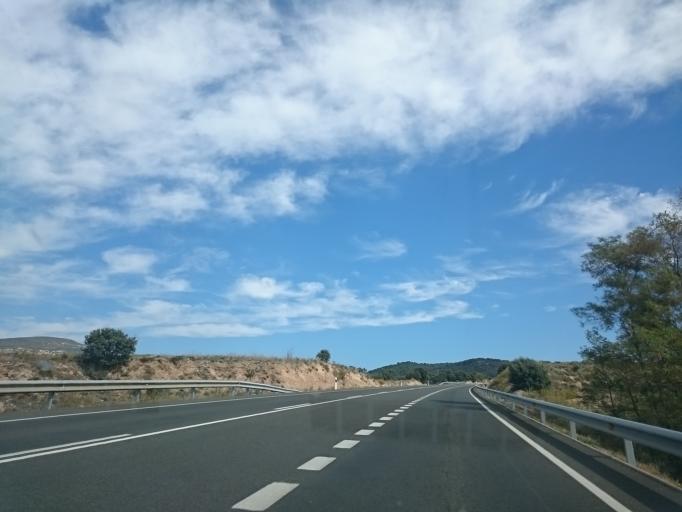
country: ES
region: Aragon
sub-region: Provincia de Huesca
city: Baells
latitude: 41.9591
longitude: 0.4728
